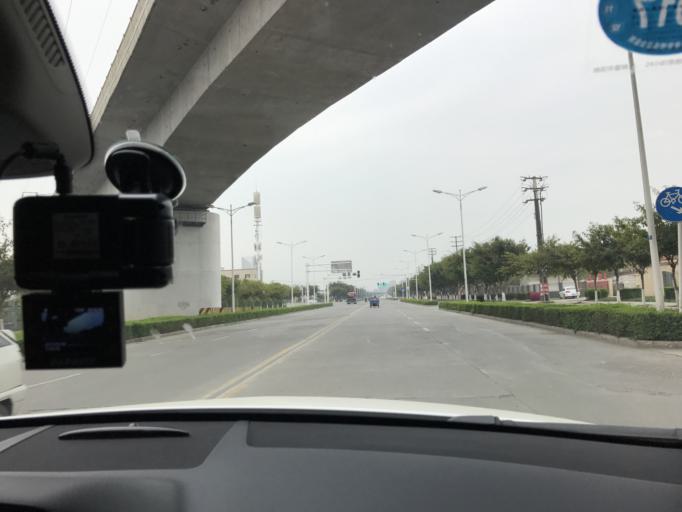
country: CN
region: Sichuan
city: Mianyang
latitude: 31.4587
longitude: 104.6831
